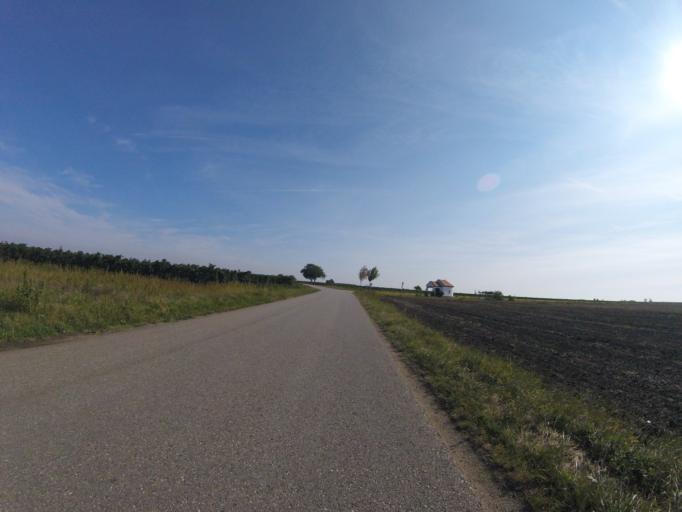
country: AT
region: Burgenland
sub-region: Politischer Bezirk Neusiedl am See
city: Illmitz
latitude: 47.7668
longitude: 16.8149
